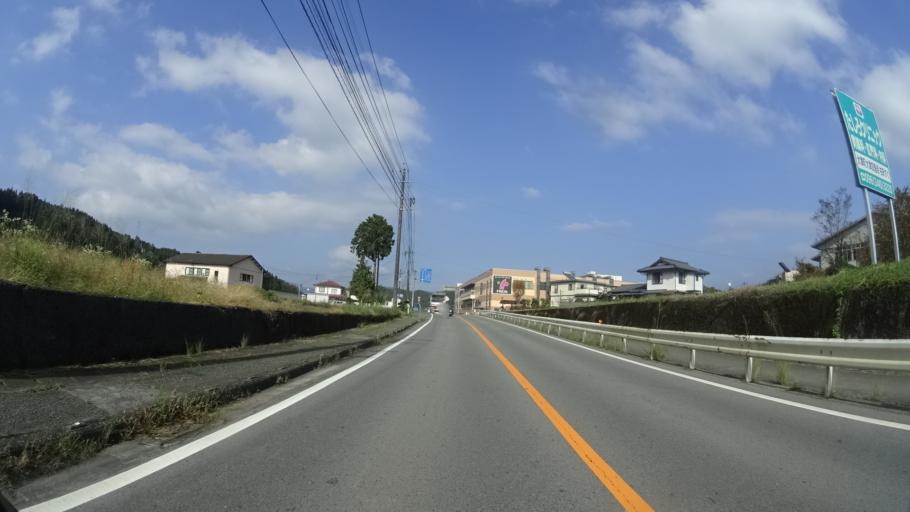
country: JP
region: Kumamoto
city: Aso
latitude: 33.1199
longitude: 131.0600
